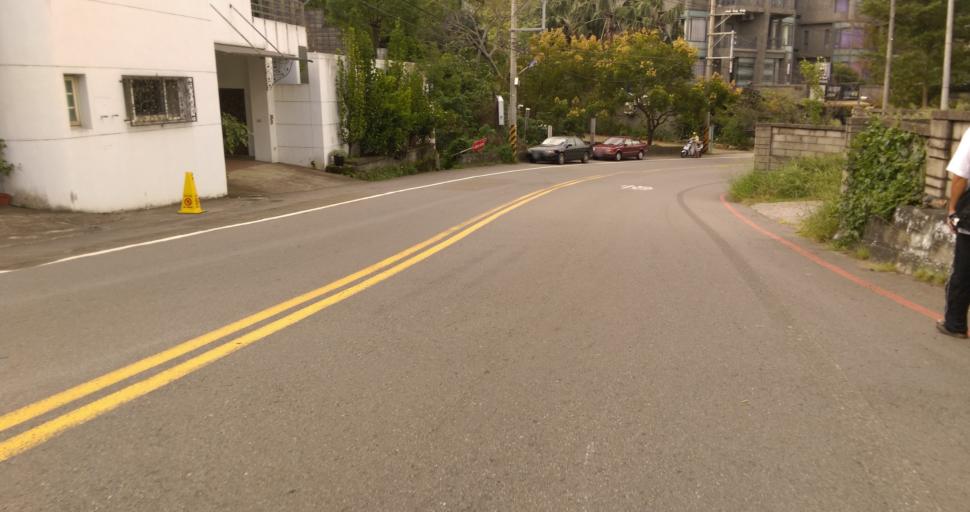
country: TW
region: Taiwan
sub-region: Hsinchu
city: Hsinchu
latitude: 24.7722
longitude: 120.9674
